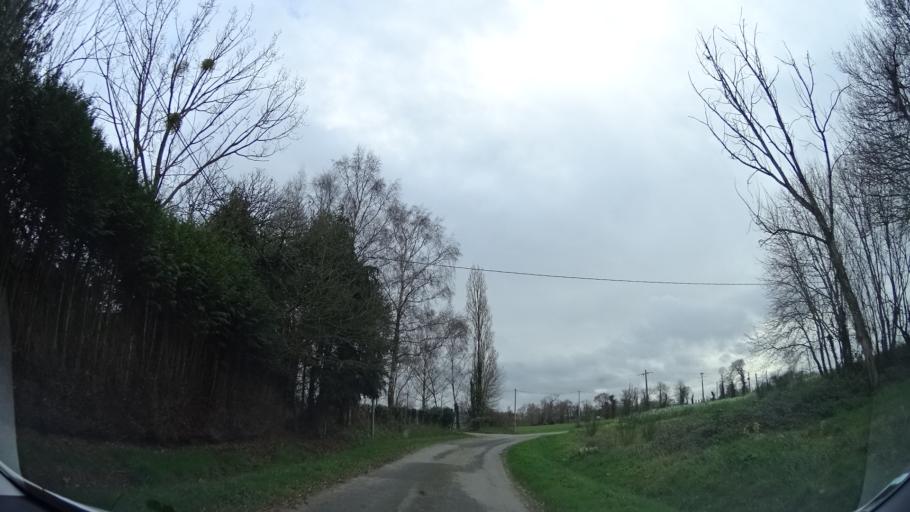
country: FR
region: Brittany
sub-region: Departement des Cotes-d'Armor
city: Evran
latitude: 48.3297
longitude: -1.9490
